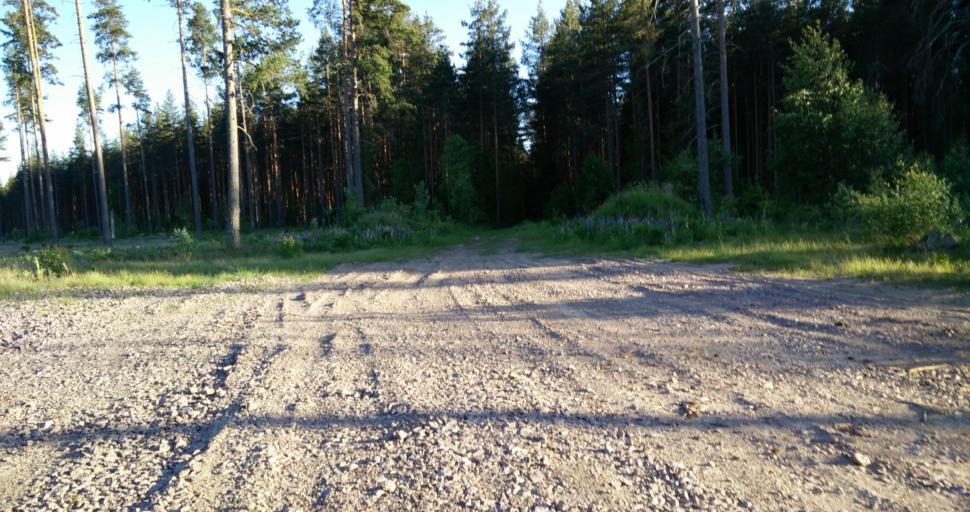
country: SE
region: Vaermland
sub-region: Hagfors Kommun
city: Hagfors
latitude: 60.0210
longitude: 13.5898
